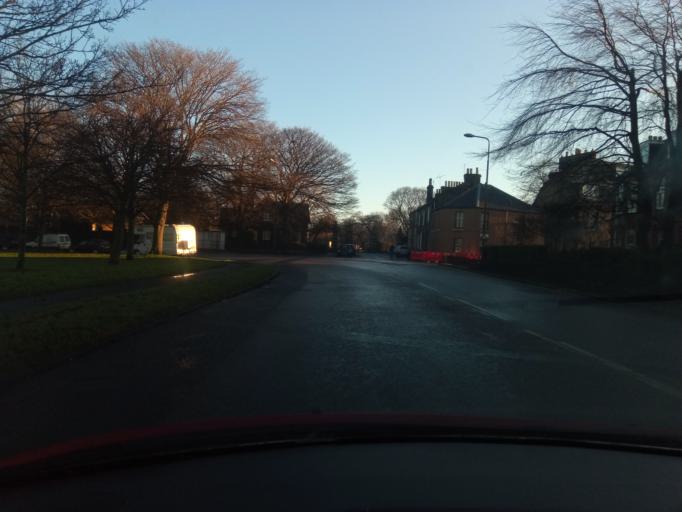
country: GB
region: Scotland
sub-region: West Lothian
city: Seafield
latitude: 55.9702
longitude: -3.1529
